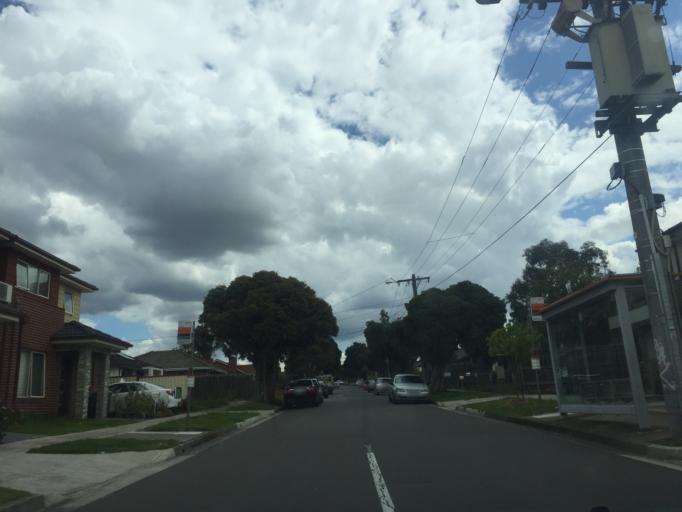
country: AU
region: Victoria
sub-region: Darebin
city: Kingsbury
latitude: -37.7124
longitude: 145.0224
